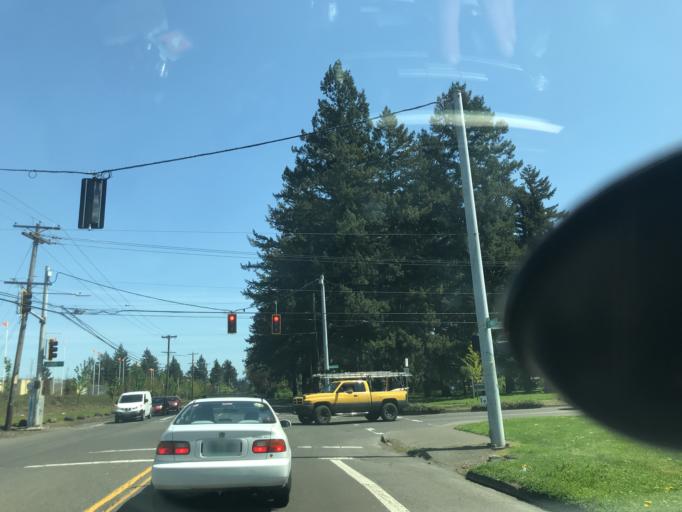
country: US
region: Oregon
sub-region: Multnomah County
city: Lents
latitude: 45.4959
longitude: -122.5564
